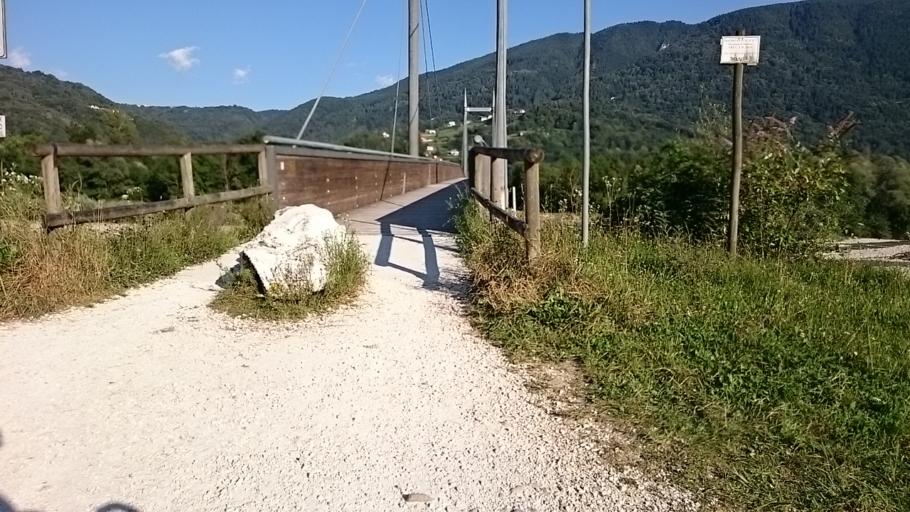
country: IT
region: Veneto
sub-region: Provincia di Belluno
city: Farra d'Alpago
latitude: 46.1207
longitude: 12.3479
